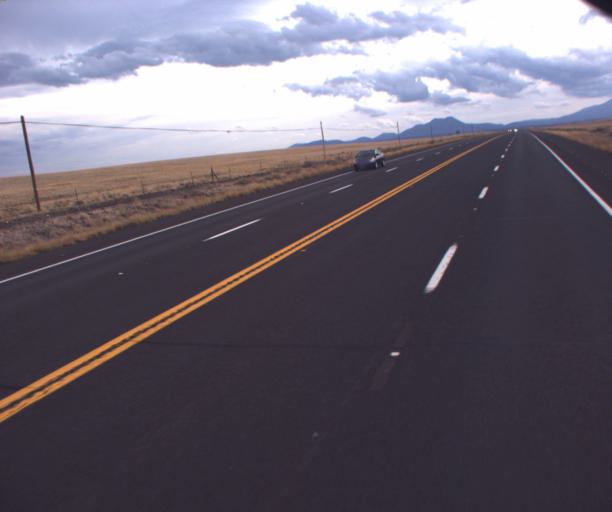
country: US
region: Arizona
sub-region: Coconino County
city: Flagstaff
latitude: 35.6334
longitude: -111.5196
